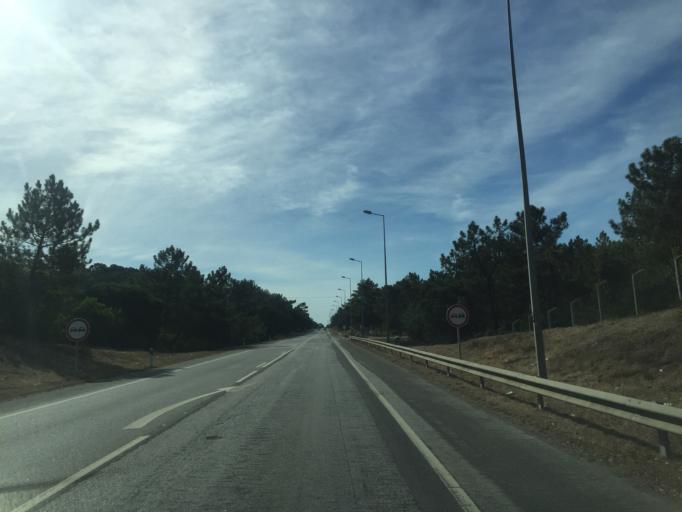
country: PT
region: Coimbra
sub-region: Figueira da Foz
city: Lavos
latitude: 40.1091
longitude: -8.8556
